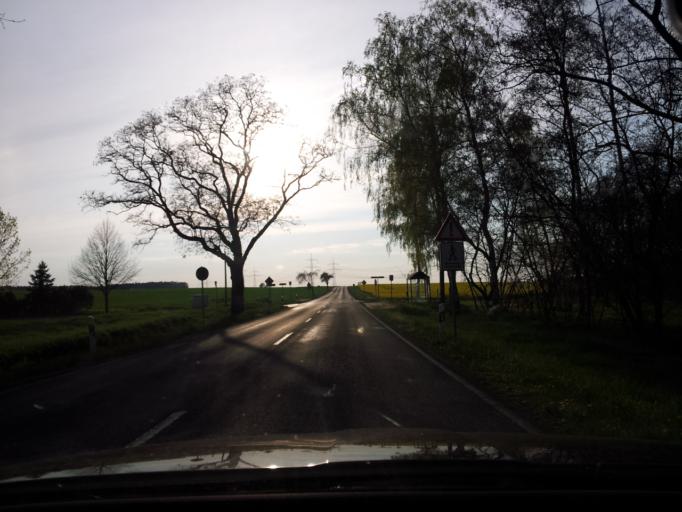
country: DE
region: Brandenburg
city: Dahme
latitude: 51.8547
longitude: 13.4913
